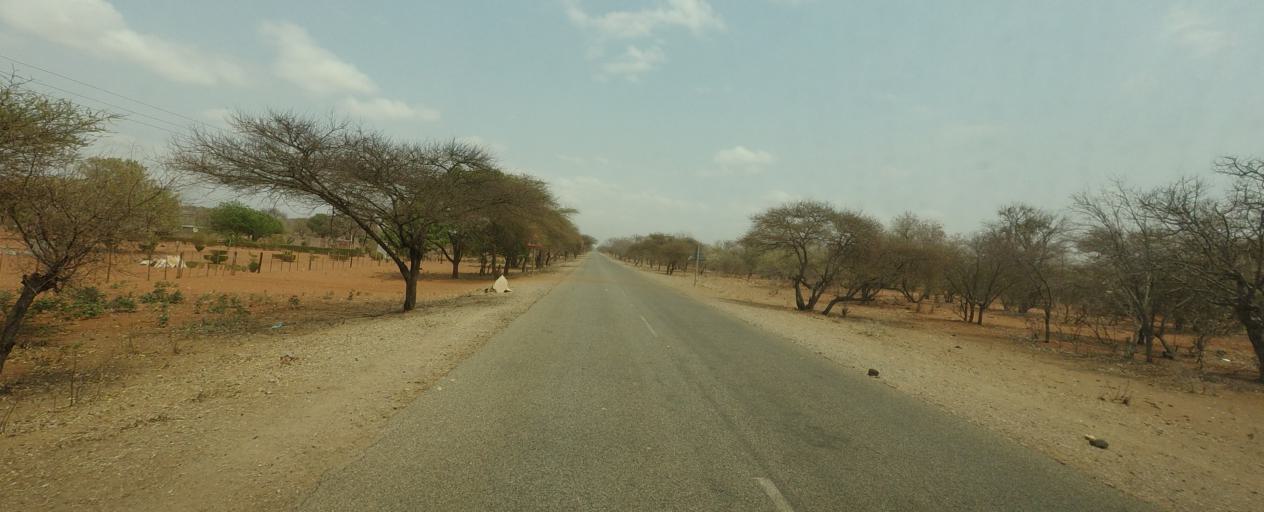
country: ZA
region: Limpopo
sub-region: Vhembe District Municipality
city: Mutale
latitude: -22.4220
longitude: 30.9067
